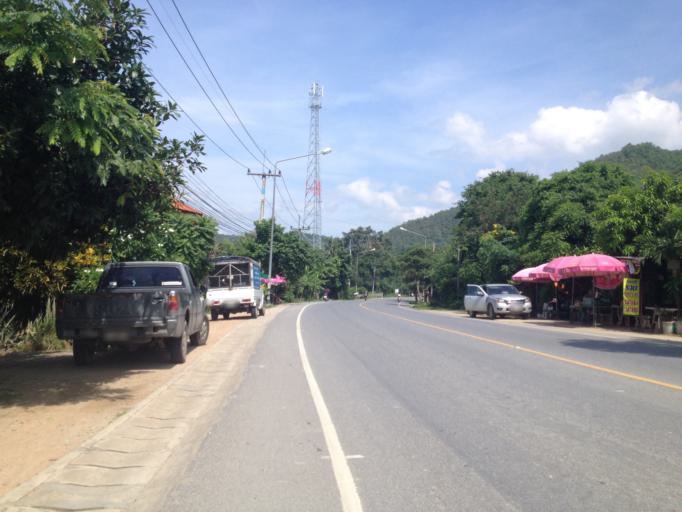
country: TH
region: Chiang Mai
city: Hang Dong
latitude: 18.7325
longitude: 98.9058
